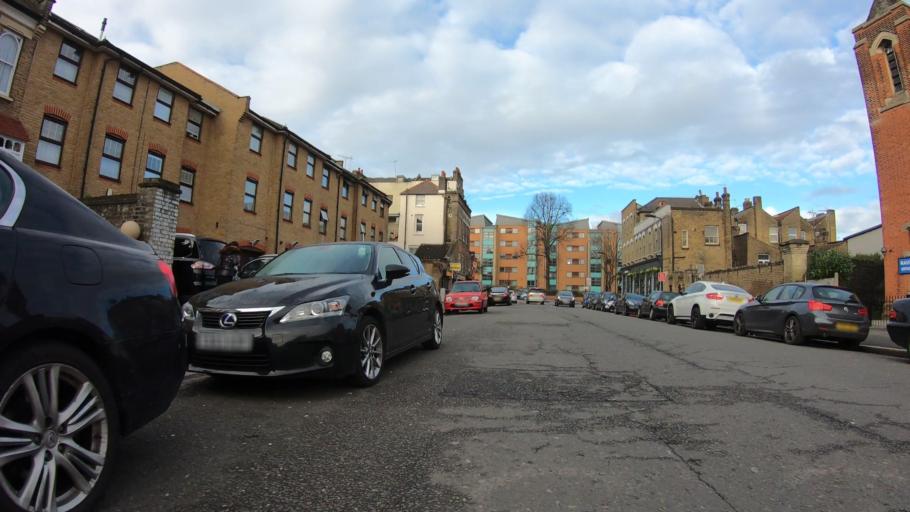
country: GB
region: England
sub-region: Greater London
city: Hackney
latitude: 51.5705
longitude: -0.0578
